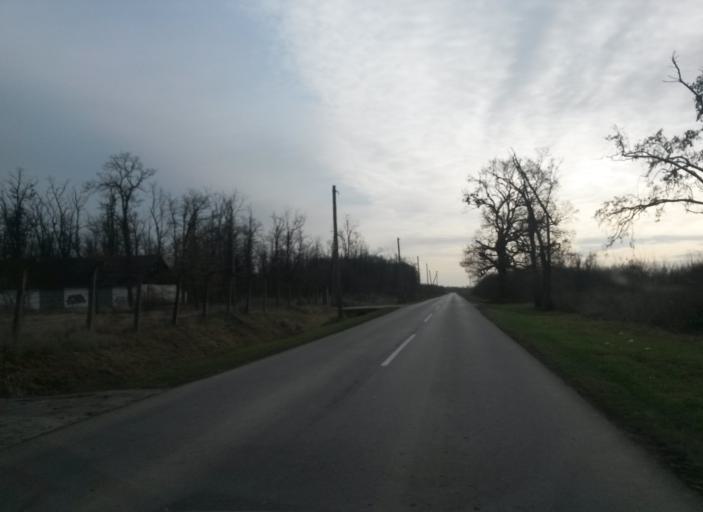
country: HR
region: Osjecko-Baranjska
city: Ovcara
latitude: 45.5137
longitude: 18.5938
